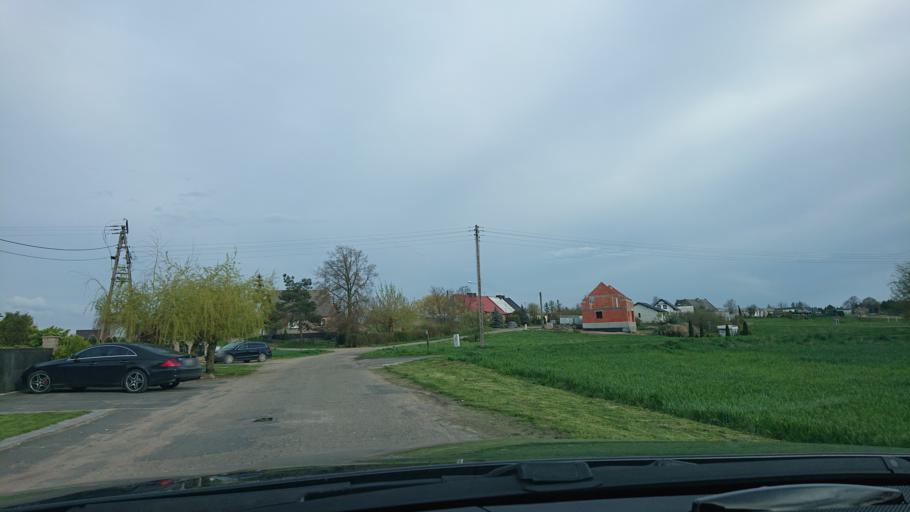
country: PL
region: Greater Poland Voivodeship
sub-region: Powiat gnieznienski
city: Lubowo
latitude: 52.5743
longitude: 17.4721
